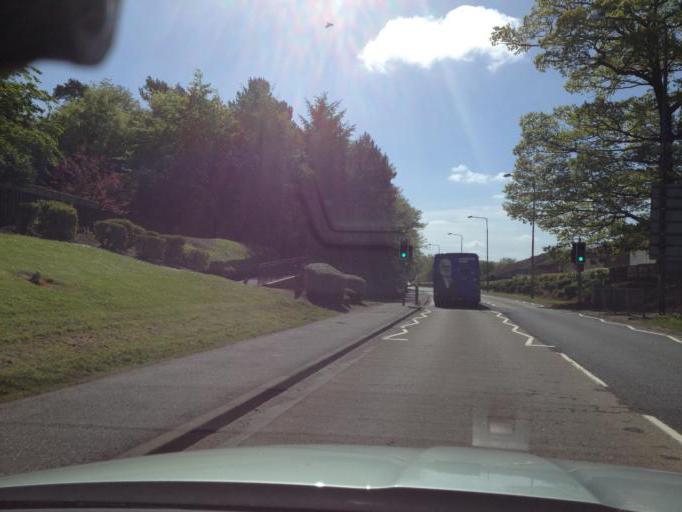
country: GB
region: Scotland
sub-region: West Lothian
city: Livingston
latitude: 55.8966
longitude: -3.5334
